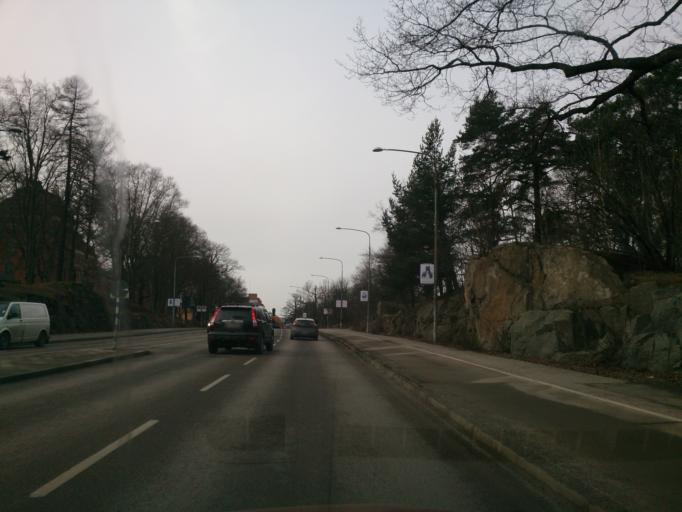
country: SE
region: Stockholm
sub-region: Stockholms Kommun
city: OEstermalm
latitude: 59.3483
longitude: 18.0911
